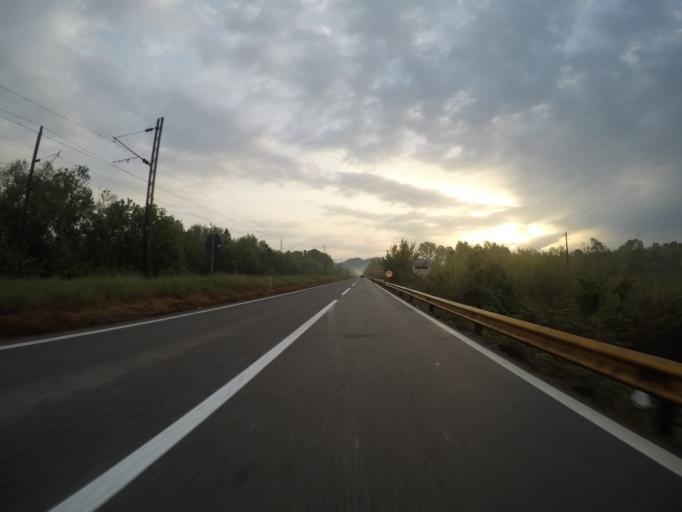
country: ME
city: Mojanovici
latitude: 42.2966
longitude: 19.1603
